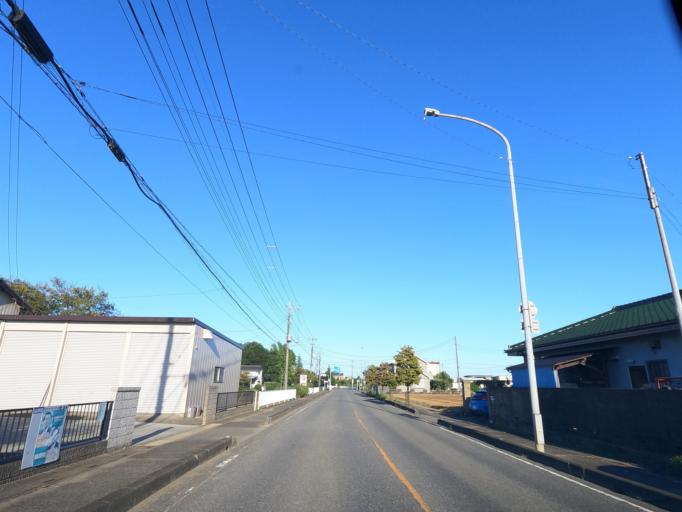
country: JP
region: Saitama
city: Kamifukuoka
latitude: 35.8821
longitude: 139.5416
